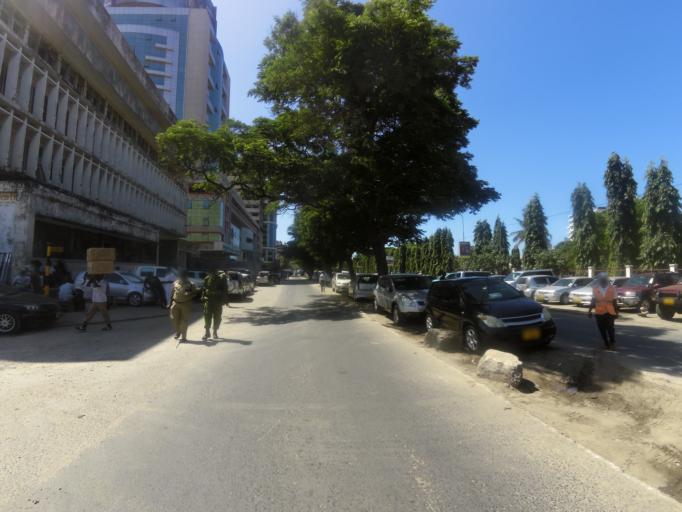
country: TZ
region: Dar es Salaam
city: Dar es Salaam
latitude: -6.8232
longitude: 39.2805
